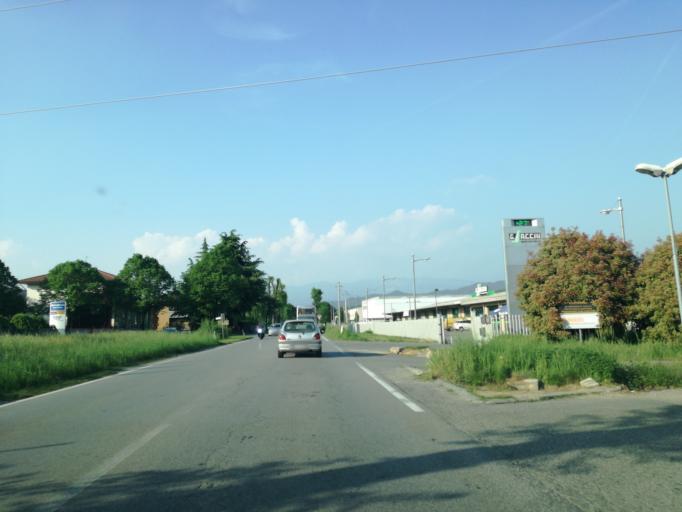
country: IT
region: Lombardy
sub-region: Provincia di Lecco
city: Robbiate
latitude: 45.6808
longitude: 9.4297
